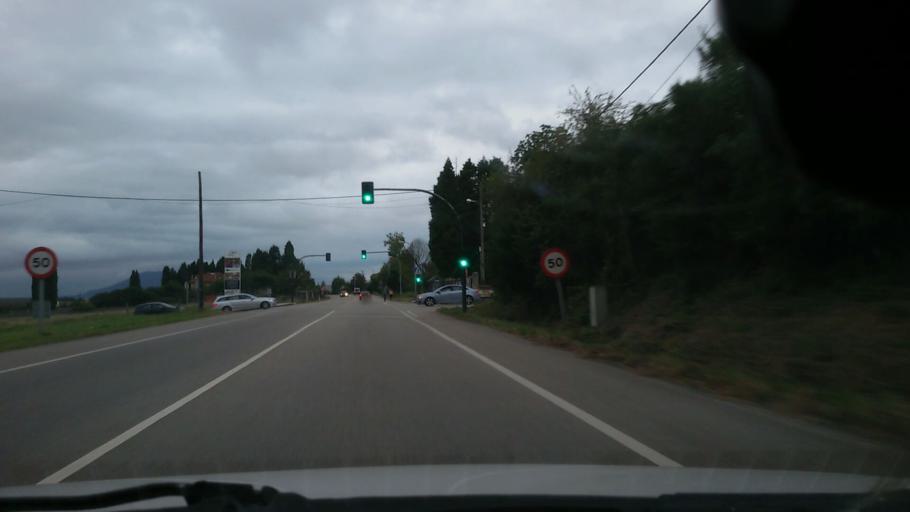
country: ES
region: Asturias
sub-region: Province of Asturias
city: Norena
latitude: 43.3852
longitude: -5.7096
